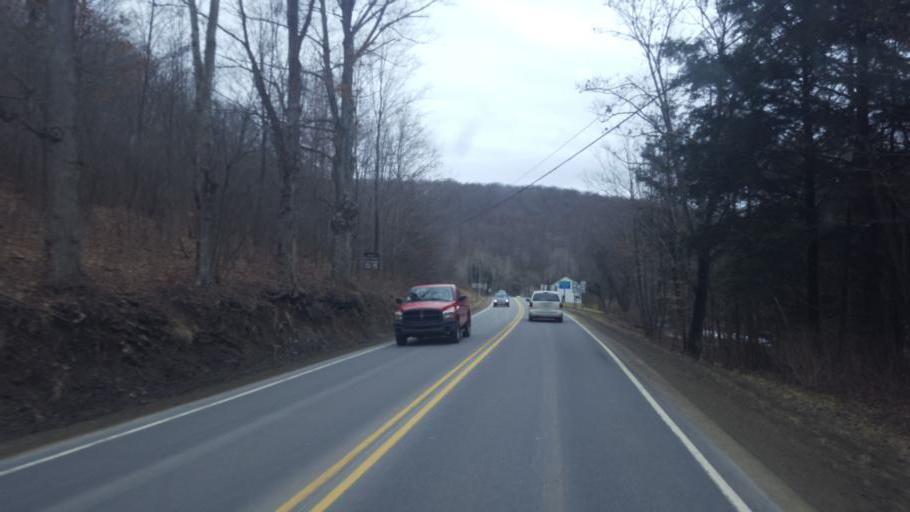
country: US
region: Pennsylvania
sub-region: Potter County
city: Coudersport
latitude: 41.8134
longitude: -78.0117
